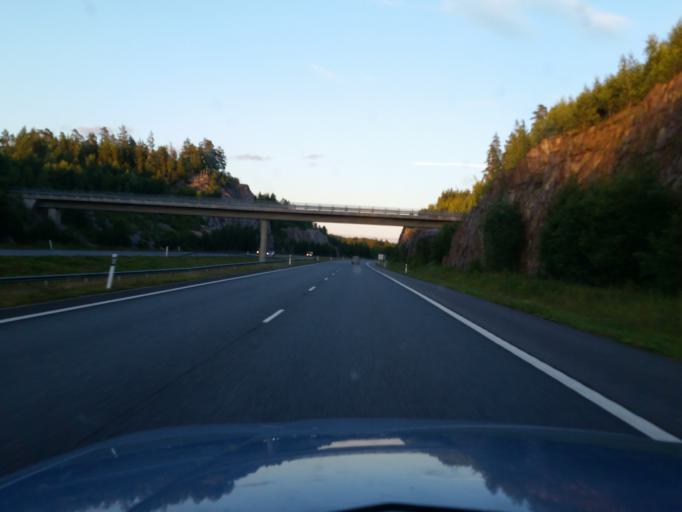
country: FI
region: Varsinais-Suomi
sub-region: Salo
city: Pertteli
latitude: 60.3990
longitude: 23.2423
